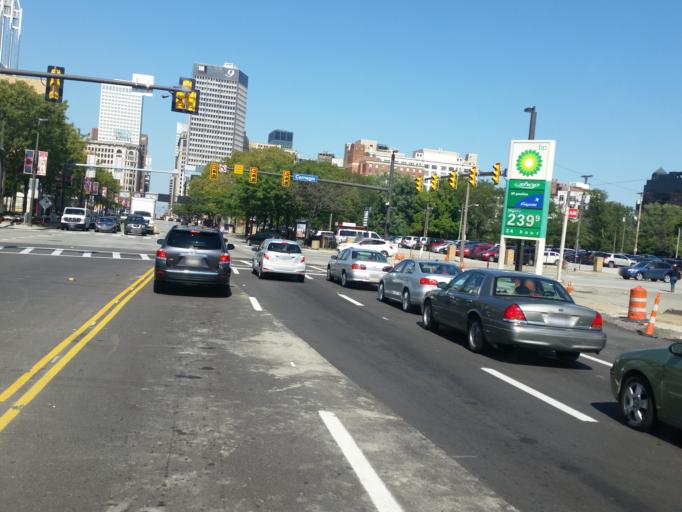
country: US
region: Ohio
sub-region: Cuyahoga County
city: Cleveland
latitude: 41.4954
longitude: -81.6824
